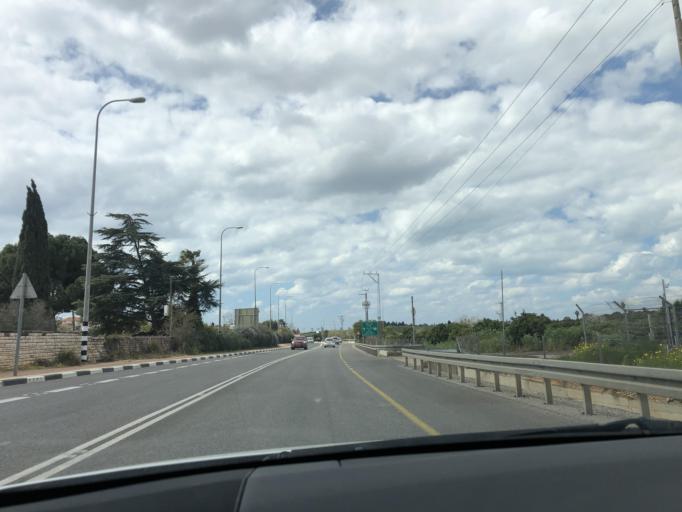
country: IL
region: Central District
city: Tel Mond
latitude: 32.2611
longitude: 34.9273
